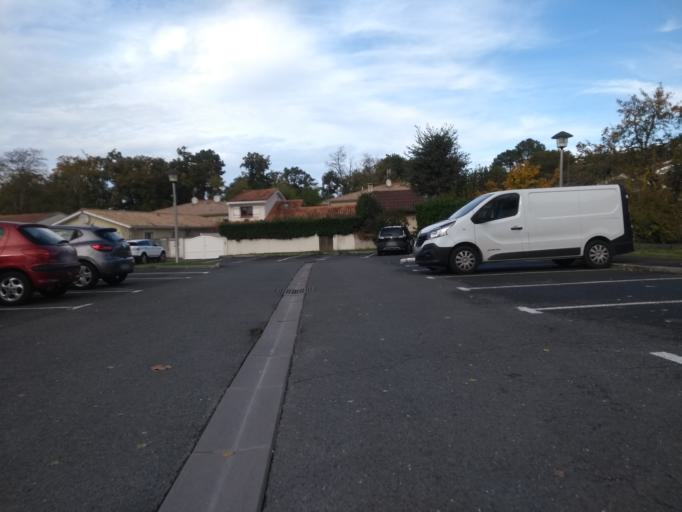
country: FR
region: Aquitaine
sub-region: Departement de la Gironde
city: Cestas
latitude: 44.7418
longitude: -0.6845
